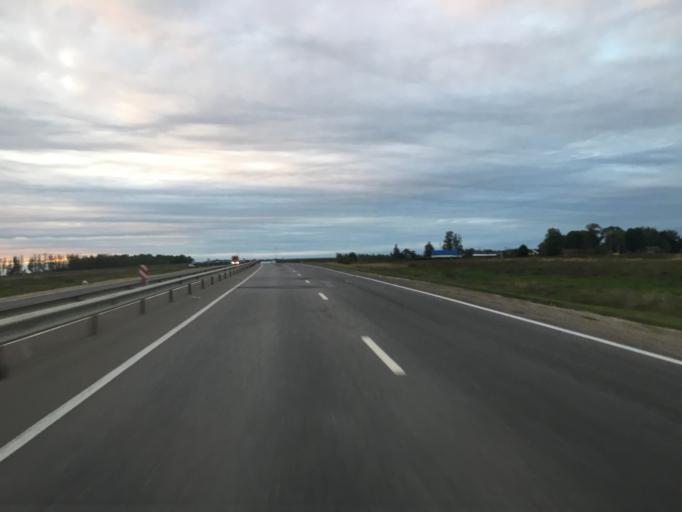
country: RU
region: Kaluga
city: Kaluga
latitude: 54.6203
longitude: 36.2944
